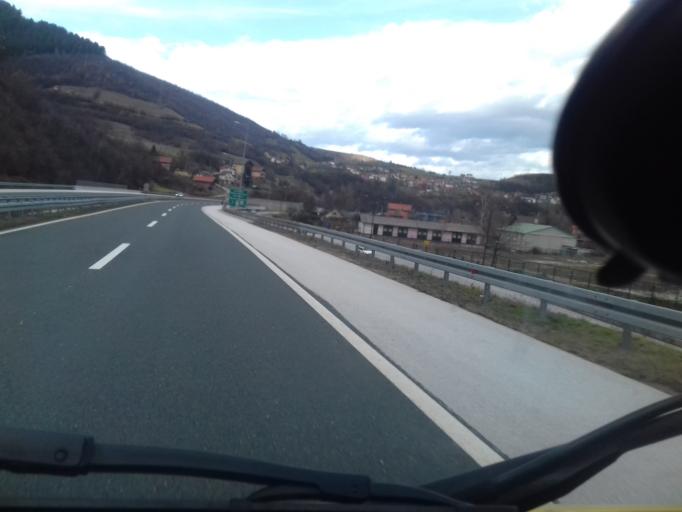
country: BA
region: Federation of Bosnia and Herzegovina
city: Kakanj
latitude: 44.0945
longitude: 18.1096
